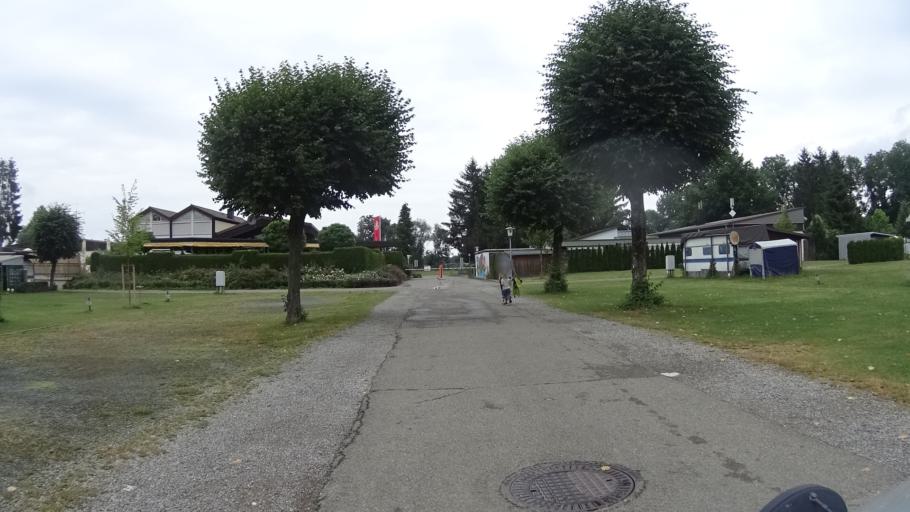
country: DE
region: Baden-Wuerttemberg
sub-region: Tuebingen Region
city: Kirchberg an der Iller
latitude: 48.1385
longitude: 10.1035
